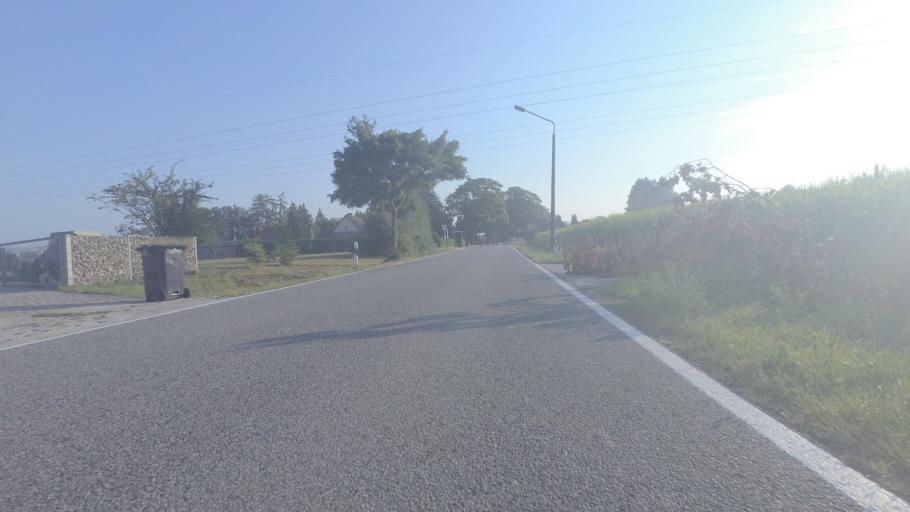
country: DE
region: Mecklenburg-Vorpommern
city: Demmin
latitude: 53.9172
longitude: 13.0654
